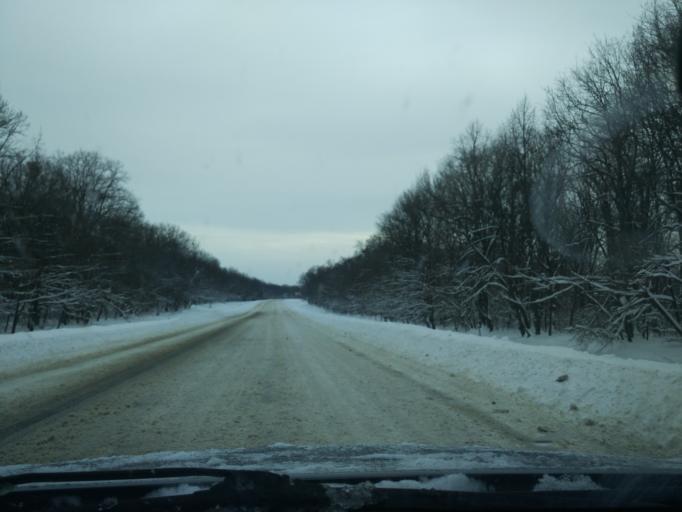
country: MD
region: Straseni
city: Straseni
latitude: 47.0321
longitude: 28.5999
